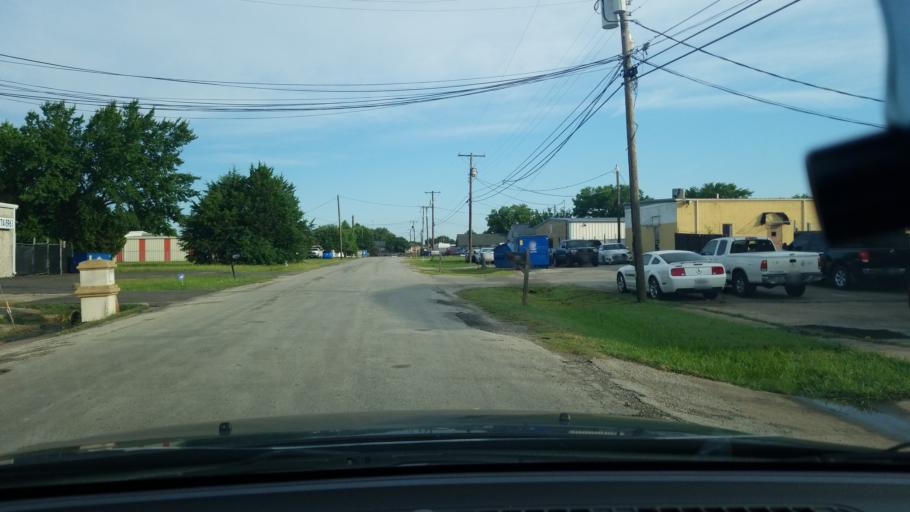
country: US
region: Texas
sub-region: Dallas County
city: Mesquite
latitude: 32.7955
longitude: -96.6204
